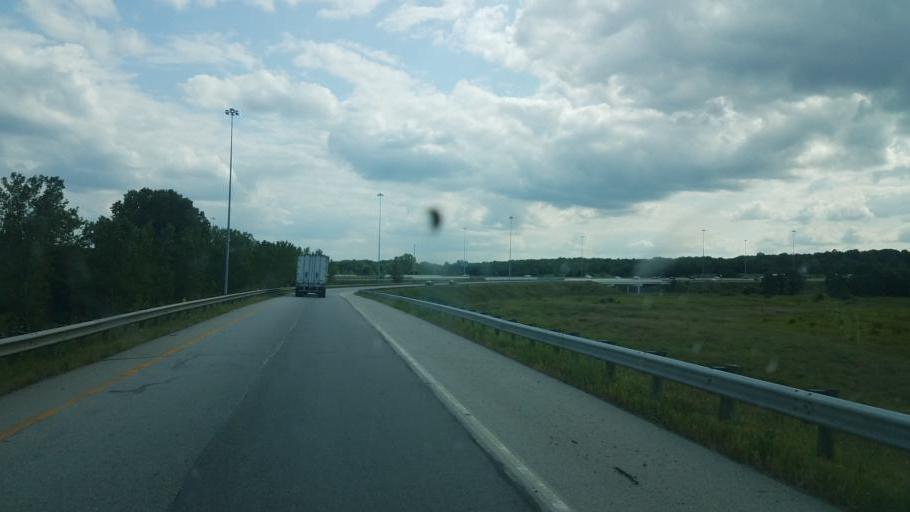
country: US
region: Ohio
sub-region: Medina County
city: Westfield Center
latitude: 41.0299
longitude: -81.9012
